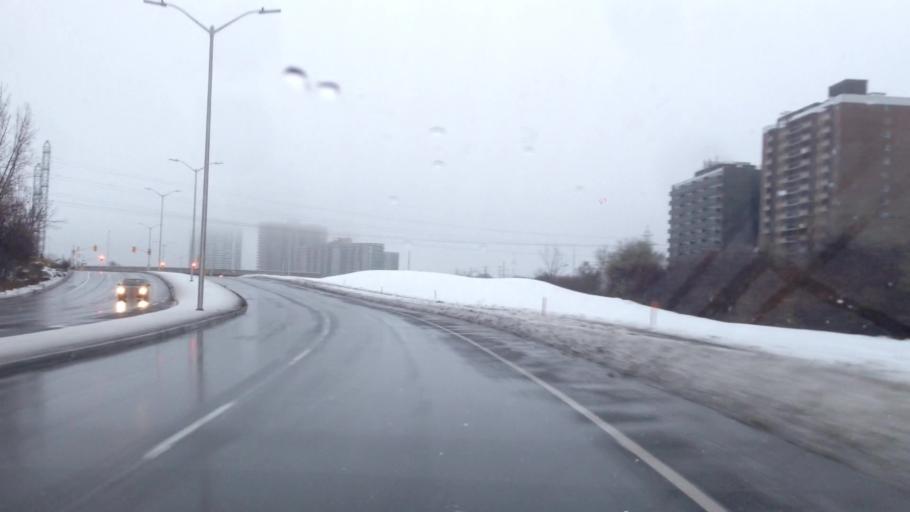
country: CA
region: Ontario
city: Ottawa
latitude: 45.4015
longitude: -75.6671
